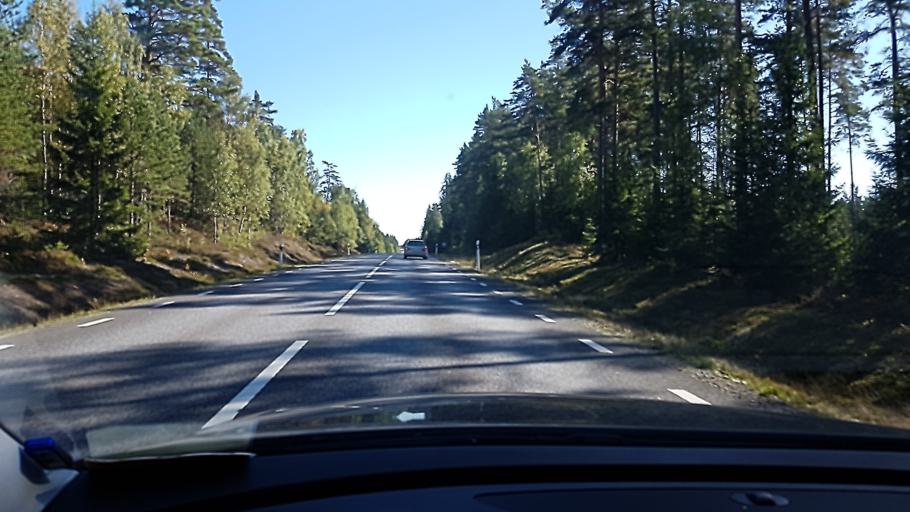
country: SE
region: Kronoberg
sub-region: Lessebo Kommun
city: Lessebo
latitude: 56.7319
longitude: 15.4113
